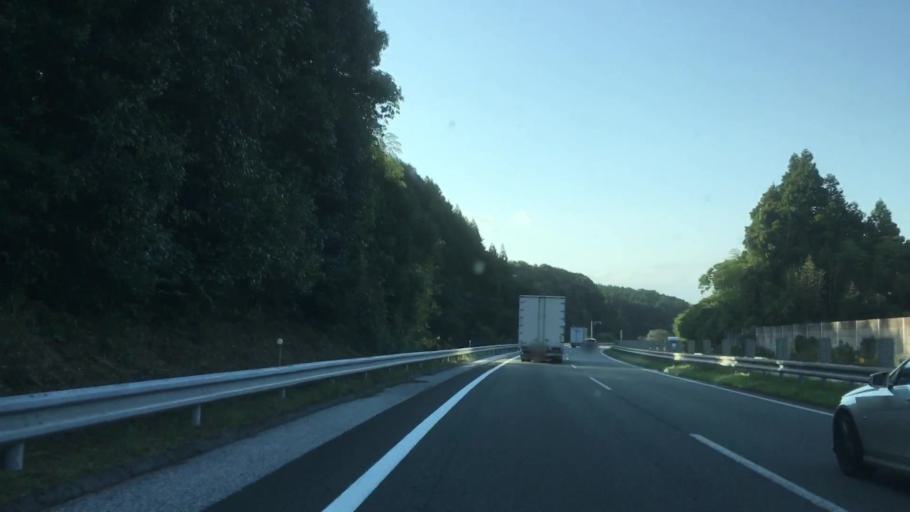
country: JP
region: Yamaguchi
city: Ogori-shimogo
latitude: 34.1453
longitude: 131.3466
